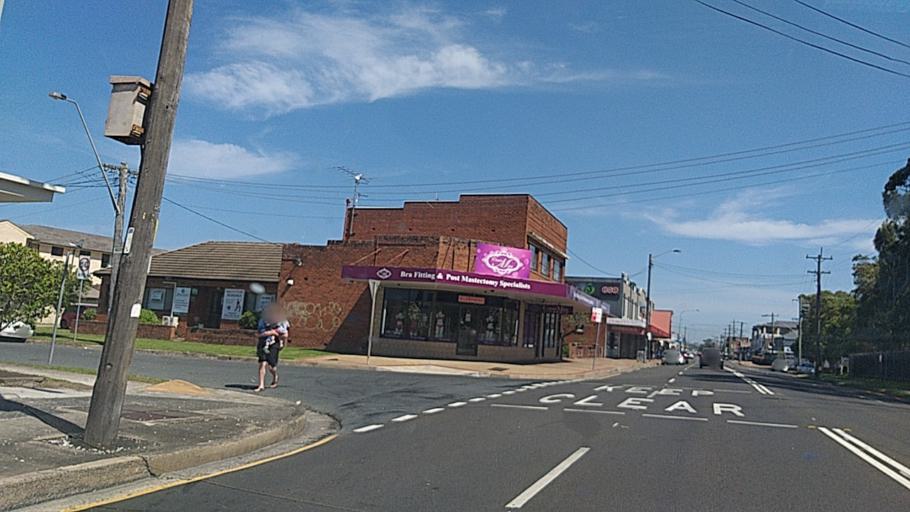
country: AU
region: New South Wales
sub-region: Wollongong
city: Fairy Meadow
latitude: -34.3905
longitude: 150.8936
